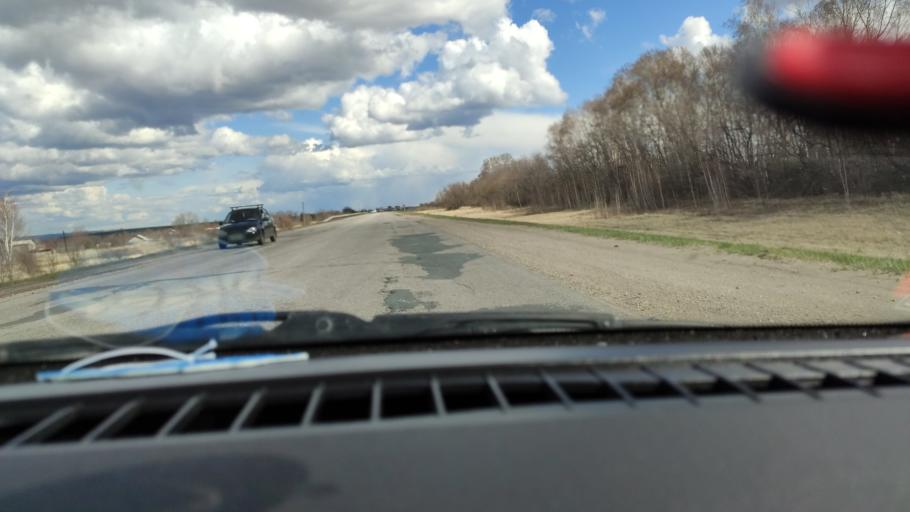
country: RU
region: Samara
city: Varlamovo
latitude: 53.1212
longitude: 48.3221
